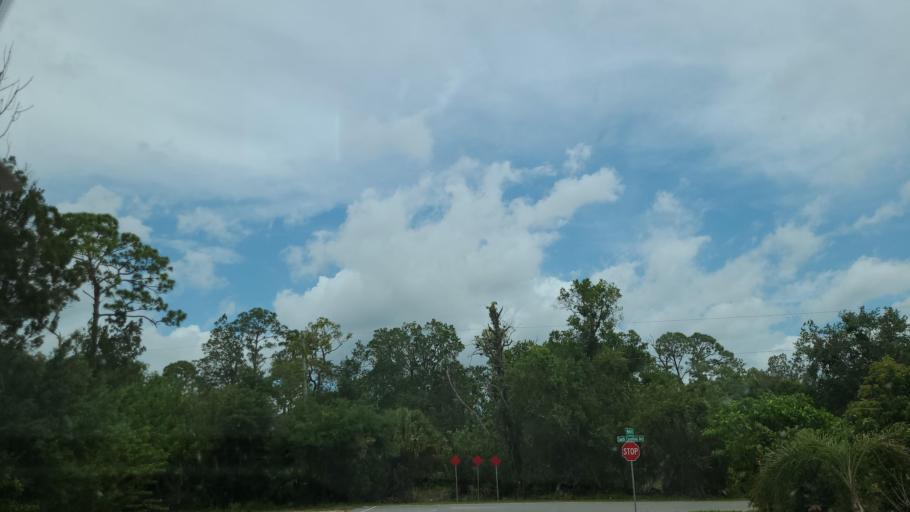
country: US
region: Florida
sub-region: Indian River County
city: Fellsmere
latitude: 27.7739
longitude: -80.6082
